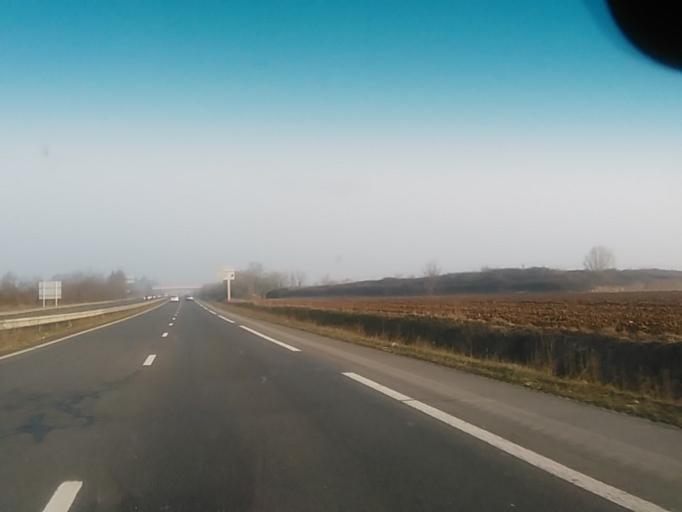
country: FR
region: Lower Normandy
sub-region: Departement du Calvados
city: Bretteville-sur-Laize
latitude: 49.0312
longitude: -0.2734
